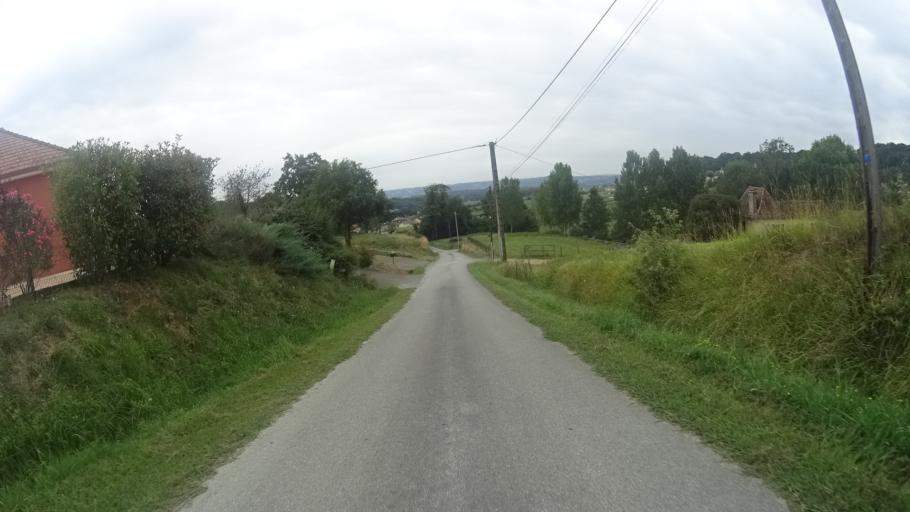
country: FR
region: Aquitaine
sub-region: Departement des Pyrenees-Atlantiques
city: Mont
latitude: 43.4932
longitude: -0.6929
